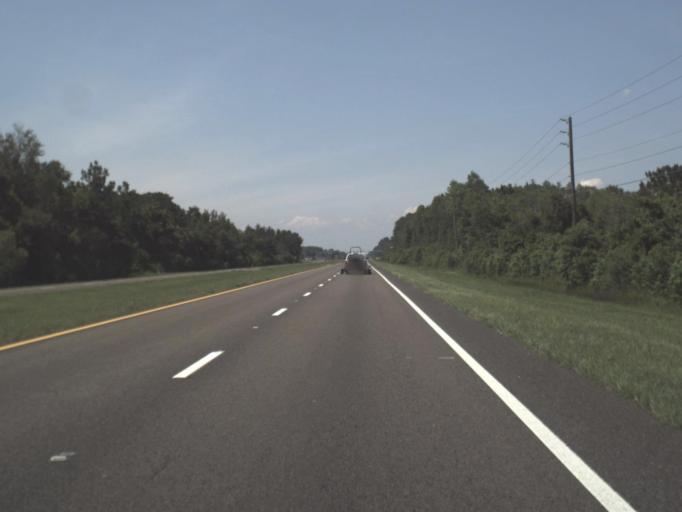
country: US
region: Florida
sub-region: Citrus County
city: Sugarmill Woods
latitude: 28.7157
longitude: -82.5525
